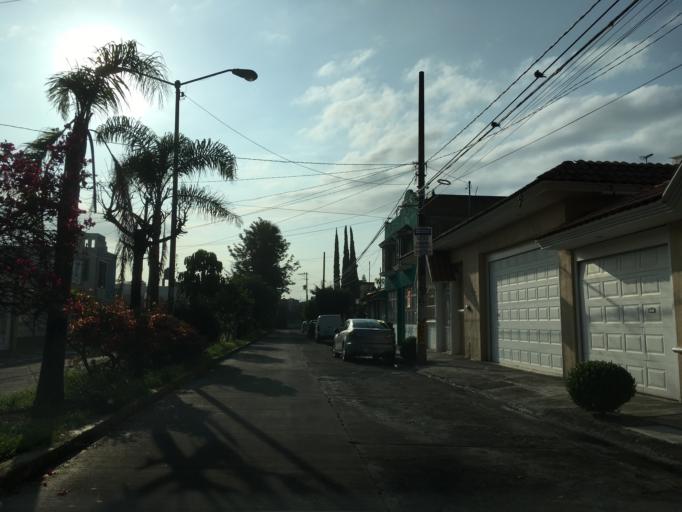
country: MX
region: Michoacan
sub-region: Morelia
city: Morelos
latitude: 19.6814
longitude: -101.2253
